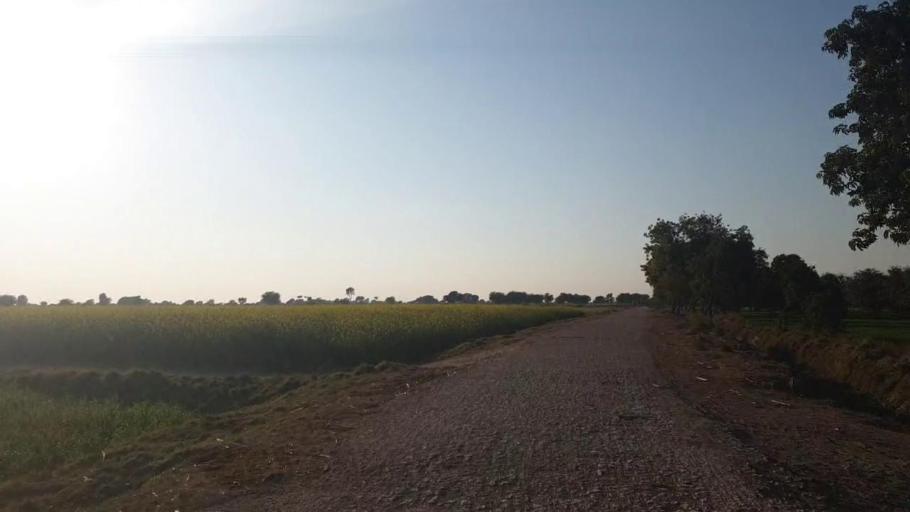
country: PK
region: Sindh
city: Shahpur Chakar
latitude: 26.0606
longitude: 68.6594
